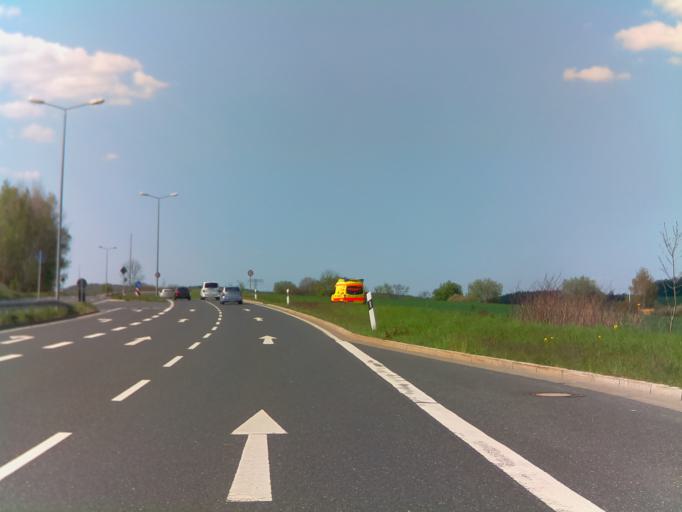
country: DE
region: Saxony
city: Plauen
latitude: 50.5026
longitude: 12.1714
